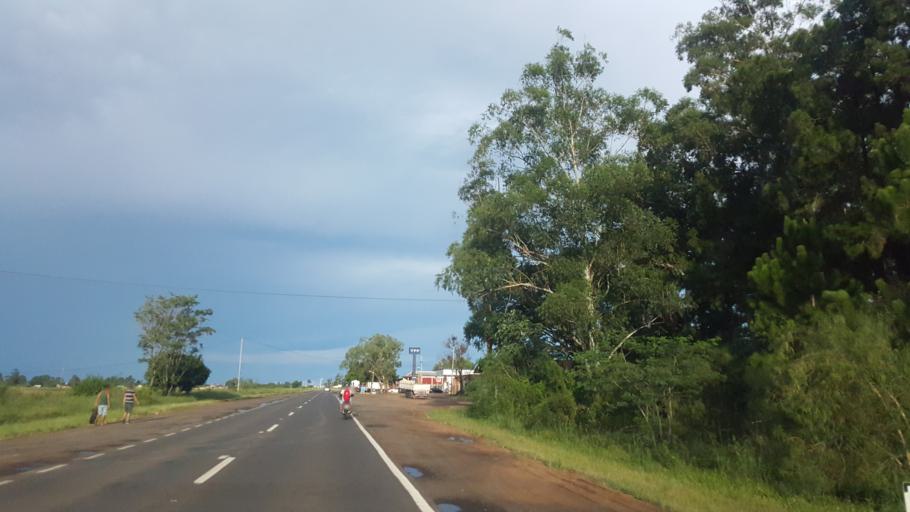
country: AR
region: Corrientes
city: Ituzaingo
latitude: -27.6057
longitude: -56.6864
